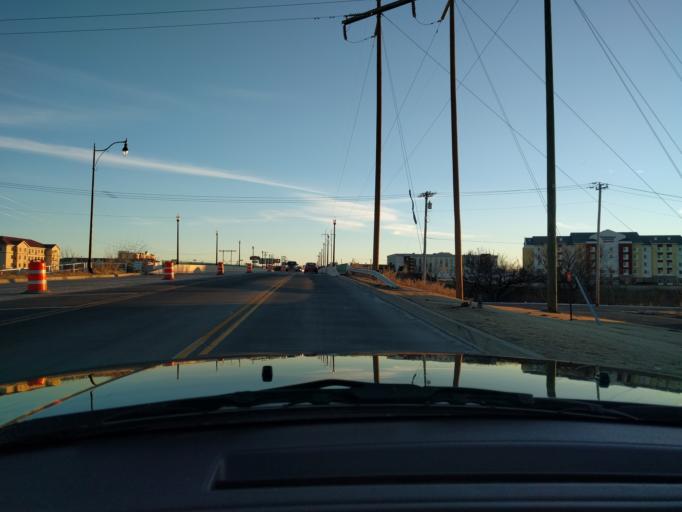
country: US
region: Oklahoma
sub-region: Oklahoma County
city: Warr Acres
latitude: 35.4508
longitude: -97.6012
